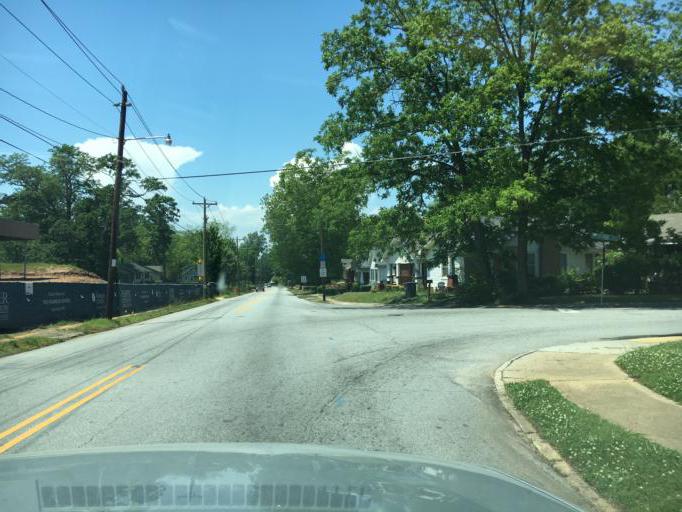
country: US
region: South Carolina
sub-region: Spartanburg County
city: Spartanburg
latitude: 34.9603
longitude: -81.9481
